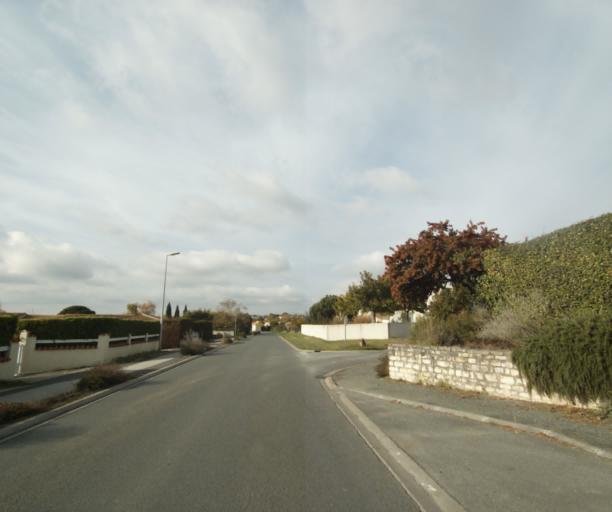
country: FR
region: Poitou-Charentes
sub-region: Departement de la Charente-Maritime
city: Saint-Georges-des-Coteaux
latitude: 45.7644
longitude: -0.7012
